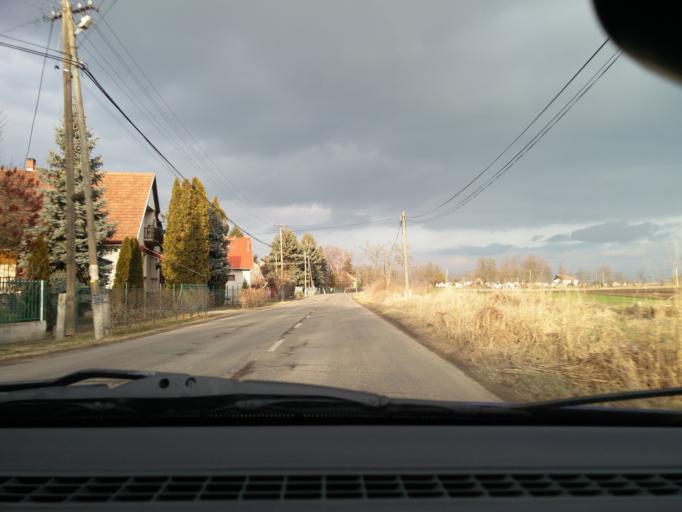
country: HU
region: Pest
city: Tapioszele
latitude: 47.3309
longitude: 19.8831
